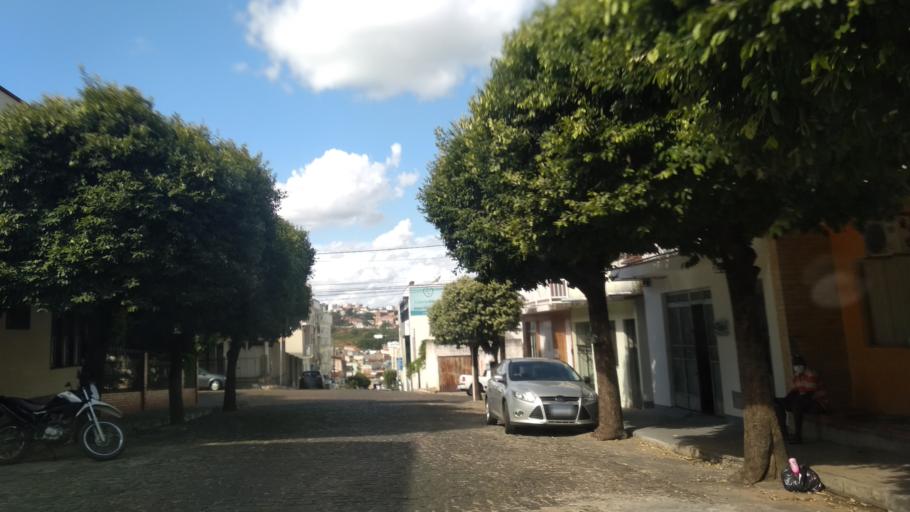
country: BR
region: Bahia
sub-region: Caetite
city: Caetite
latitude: -14.0674
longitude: -42.4923
